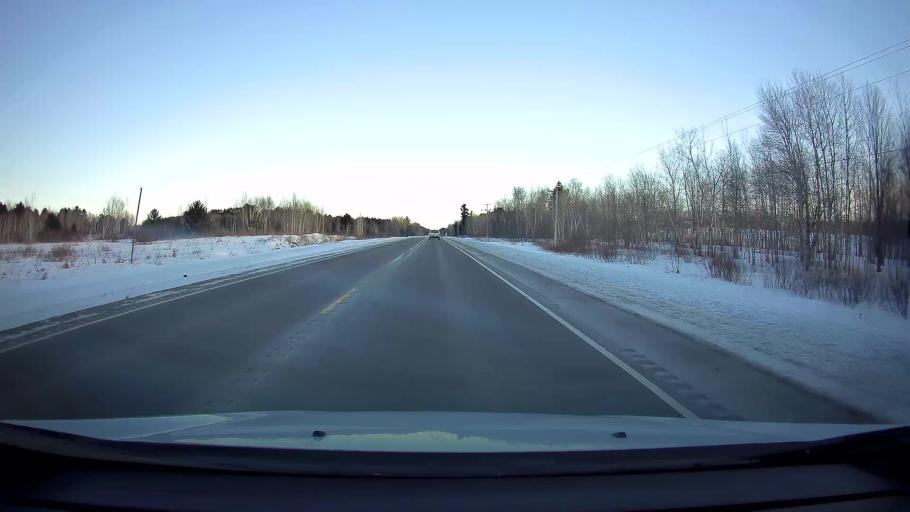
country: US
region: Wisconsin
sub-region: Washburn County
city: Shell Lake
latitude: 45.7153
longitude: -91.9410
